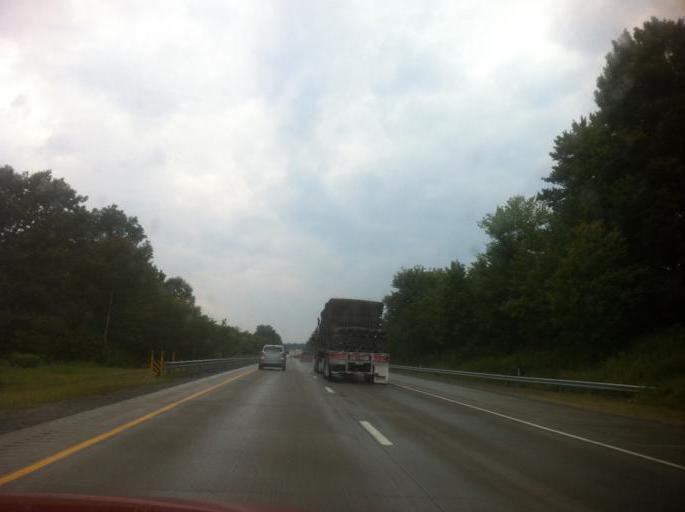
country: US
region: Pennsylvania
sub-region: Jefferson County
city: Falls Creek
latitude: 41.1536
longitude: -78.8081
